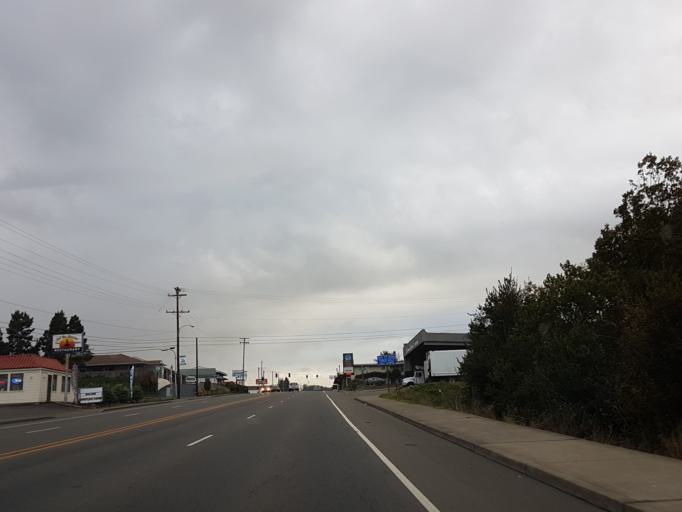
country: US
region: Oregon
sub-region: Douglas County
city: Reedsport
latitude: 43.6968
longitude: -124.1159
